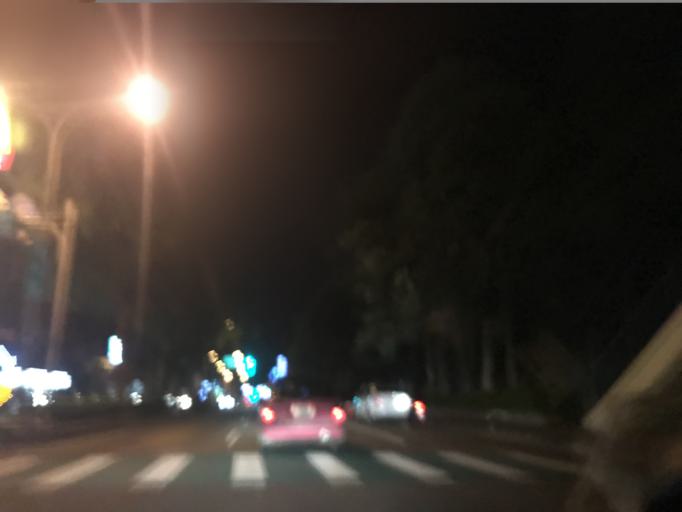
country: TW
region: Taiwan
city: Daxi
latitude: 24.8814
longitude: 121.2117
